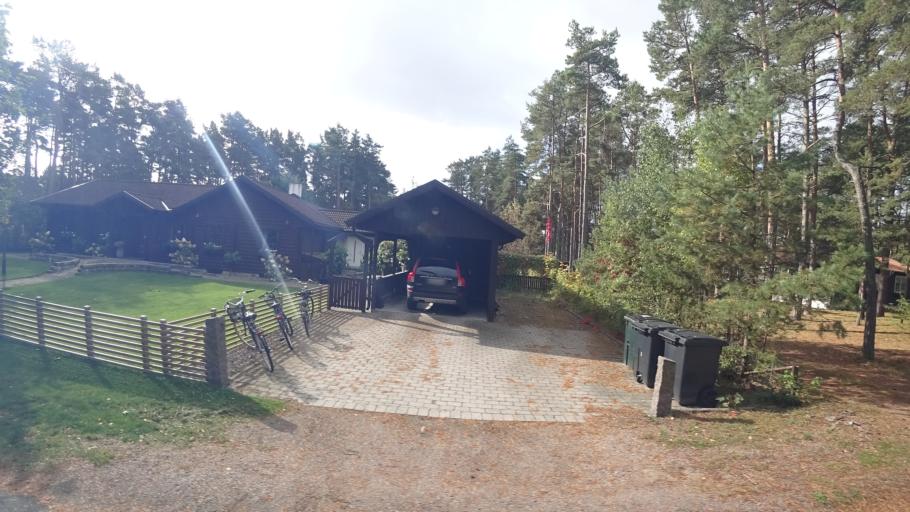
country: SE
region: Skane
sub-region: Kristianstads Kommun
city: Ahus
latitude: 55.9394
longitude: 14.3030
